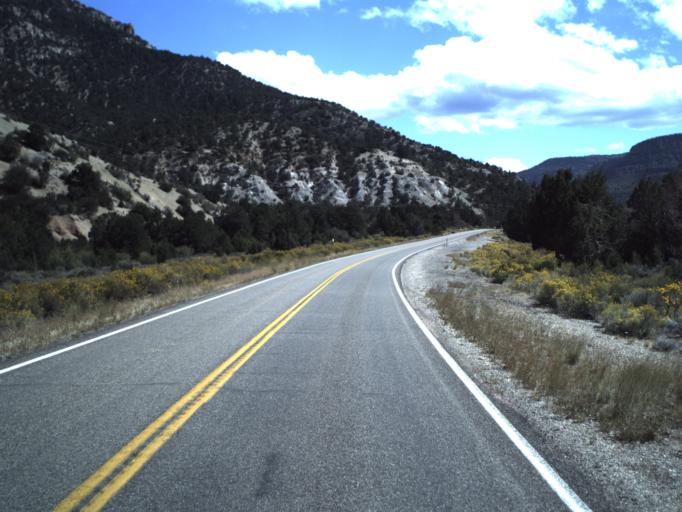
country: US
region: Utah
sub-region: Iron County
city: Cedar City
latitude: 37.6649
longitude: -113.0001
